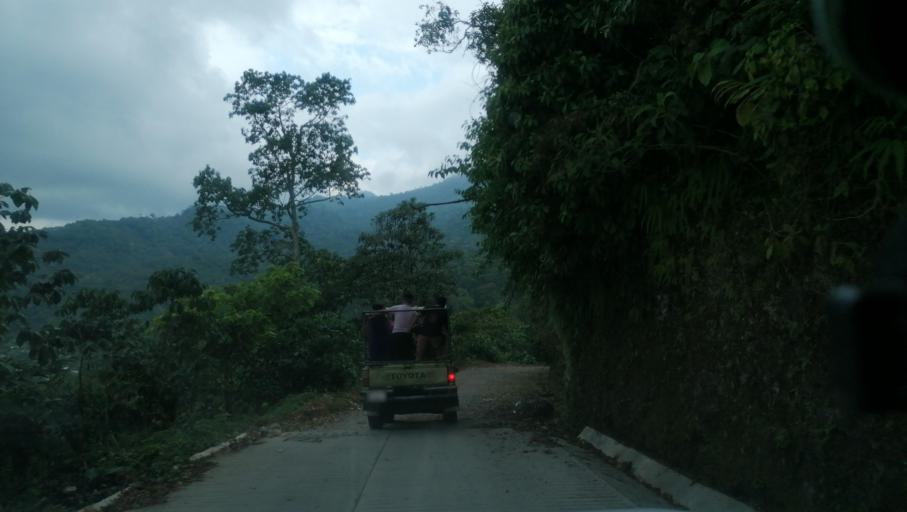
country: MX
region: Chiapas
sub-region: Cacahoatan
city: Benito Juarez
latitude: 15.0719
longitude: -92.1662
